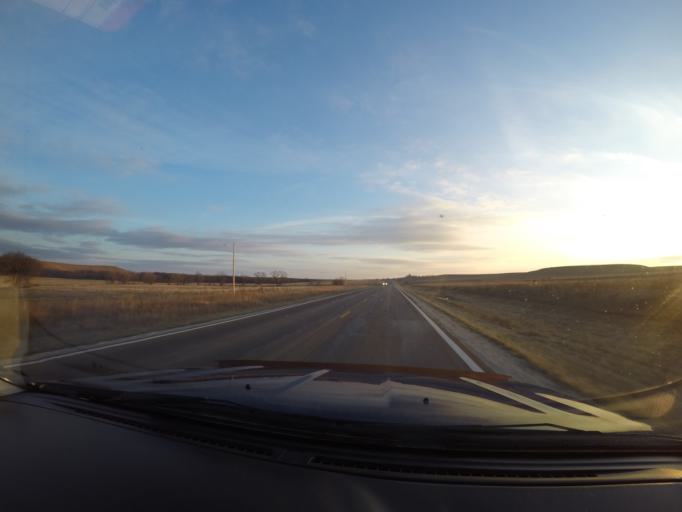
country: US
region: Kansas
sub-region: Chase County
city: Cottonwood Falls
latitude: 38.4209
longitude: -96.5571
